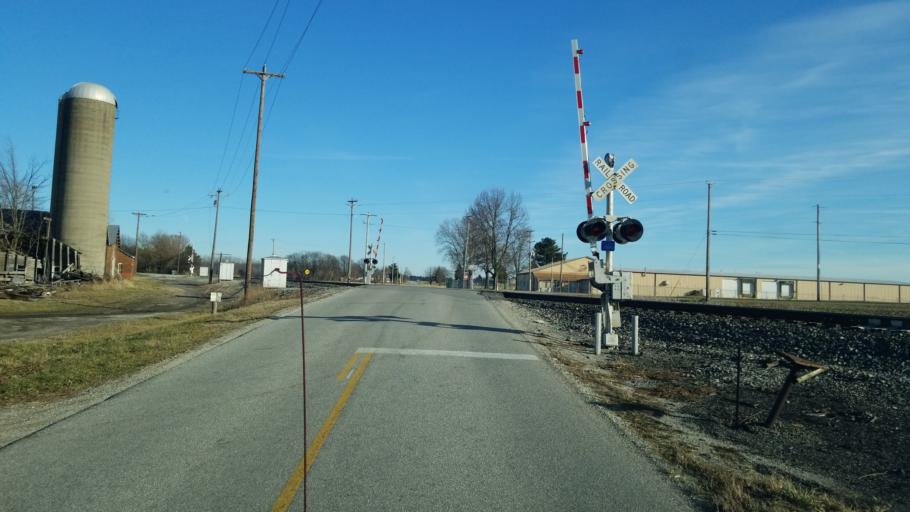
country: US
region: Ohio
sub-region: Sandusky County
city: Green Springs
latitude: 41.2559
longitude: -83.0136
